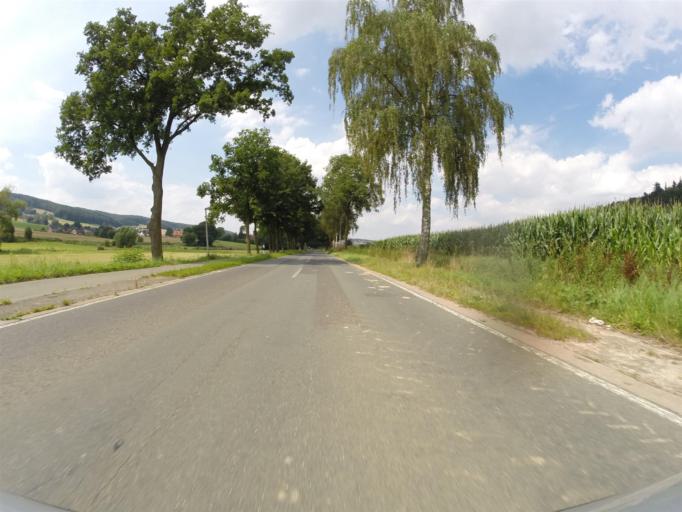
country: DE
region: North Rhine-Westphalia
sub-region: Regierungsbezirk Detmold
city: Rodinghausen
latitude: 52.2764
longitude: 8.4946
